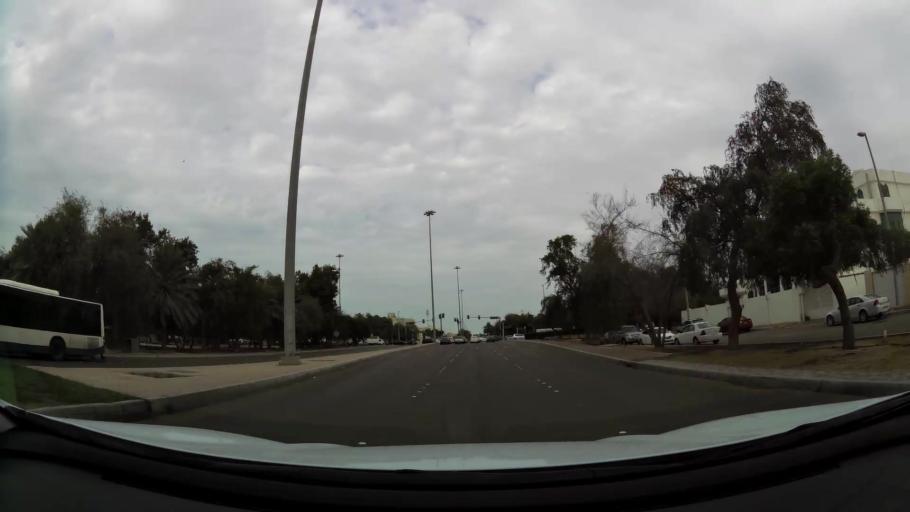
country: AE
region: Abu Dhabi
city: Abu Dhabi
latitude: 24.4351
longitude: 54.4042
